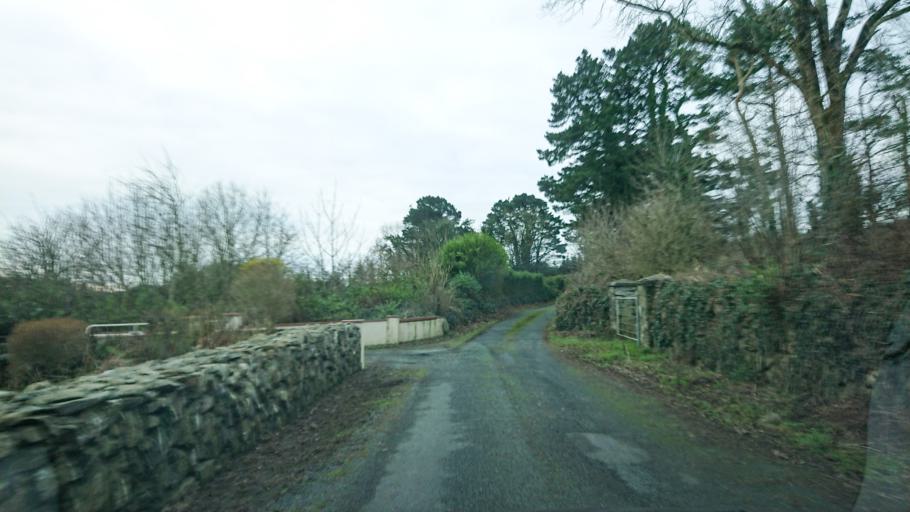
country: IE
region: Leinster
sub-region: Kilkenny
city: Mooncoin
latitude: 52.2165
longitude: -7.2712
